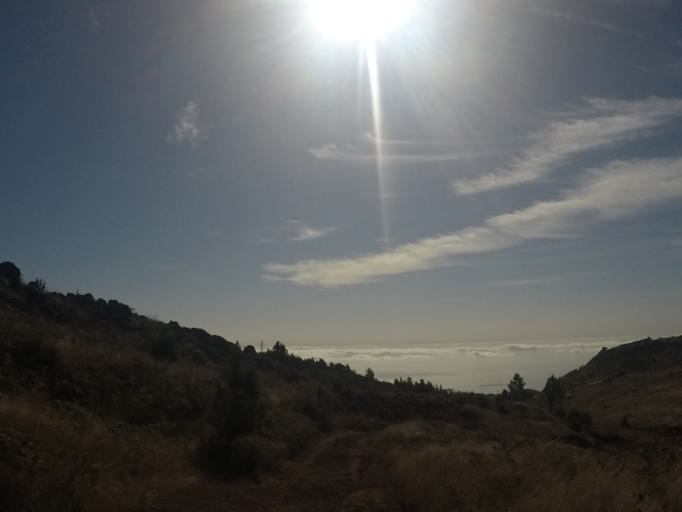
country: PT
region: Madeira
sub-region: Funchal
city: Nossa Senhora do Monte
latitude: 32.7033
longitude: -16.8989
